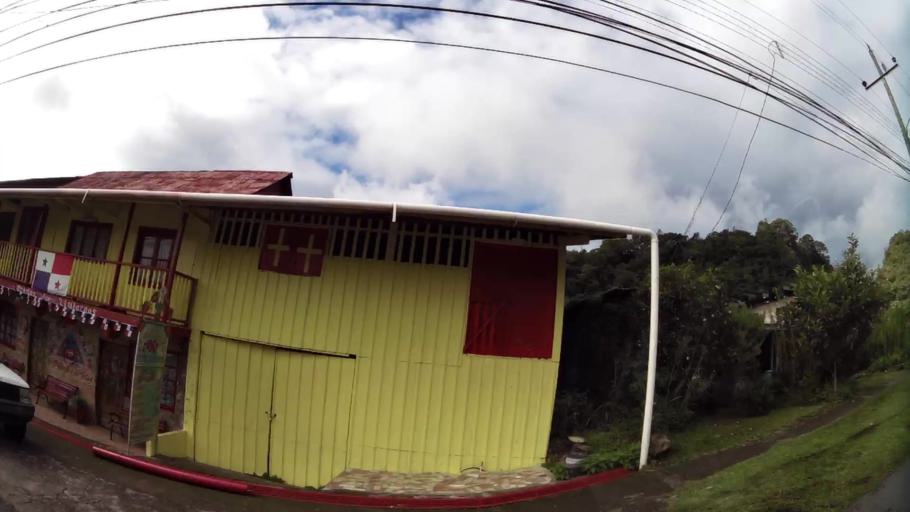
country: PA
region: Chiriqui
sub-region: Distrito Boquete
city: Boquete
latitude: 8.7949
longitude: -82.4461
